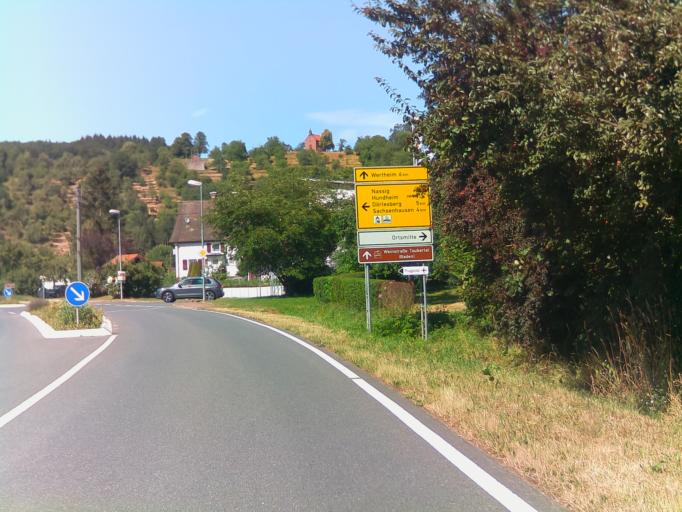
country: DE
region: Baden-Wuerttemberg
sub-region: Regierungsbezirk Stuttgart
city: Wertheim
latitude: 49.7263
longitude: 9.5319
